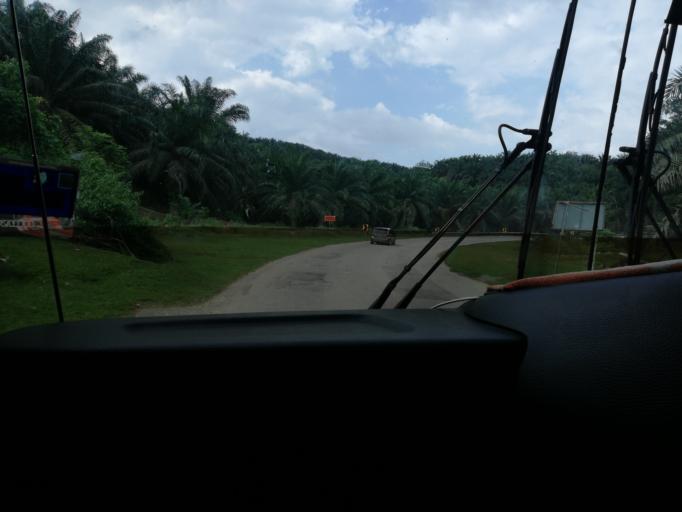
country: MY
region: Kedah
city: Kulim
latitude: 5.3333
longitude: 100.5874
